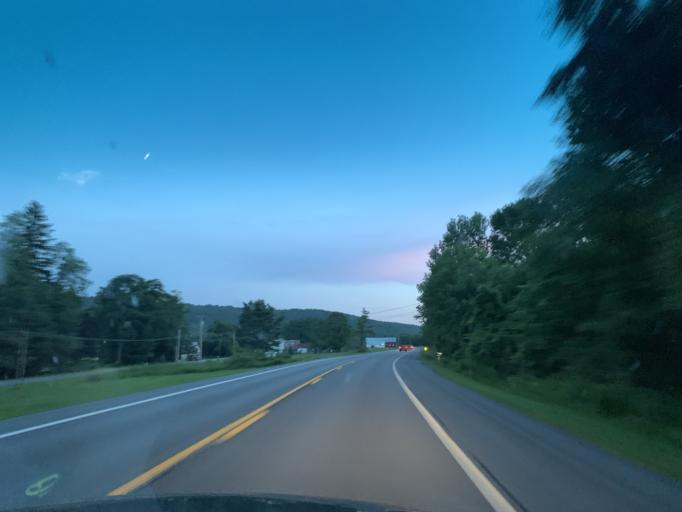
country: US
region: New York
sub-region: Chenango County
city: New Berlin
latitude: 42.5721
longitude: -75.3395
